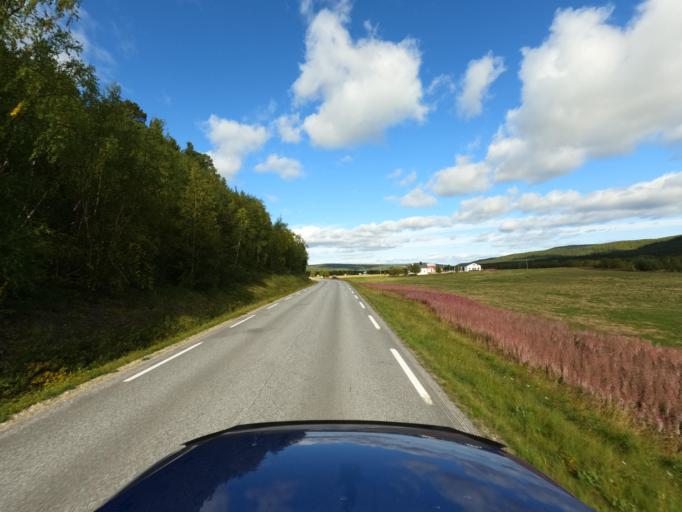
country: NO
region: Finnmark Fylke
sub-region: Karasjok
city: Karasjohka
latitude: 69.4090
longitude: 25.8063
